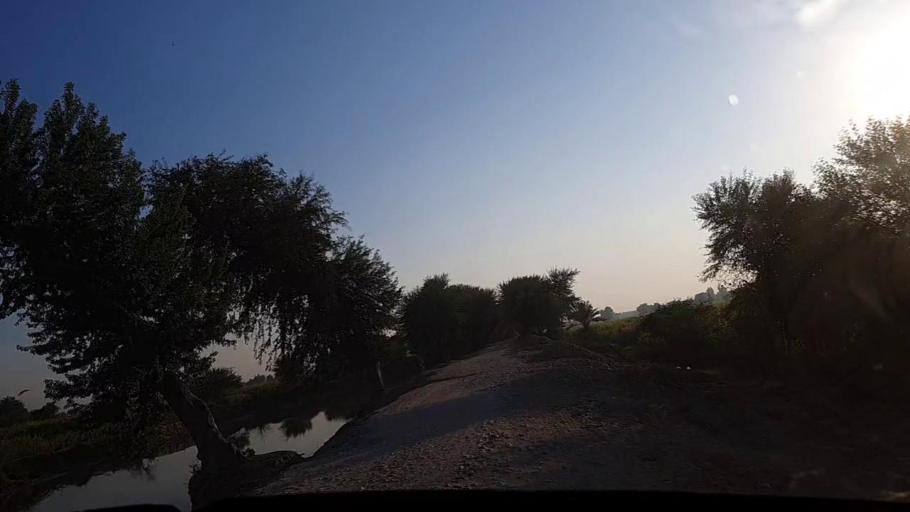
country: PK
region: Sindh
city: Sobhadero
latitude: 27.3996
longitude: 68.3887
